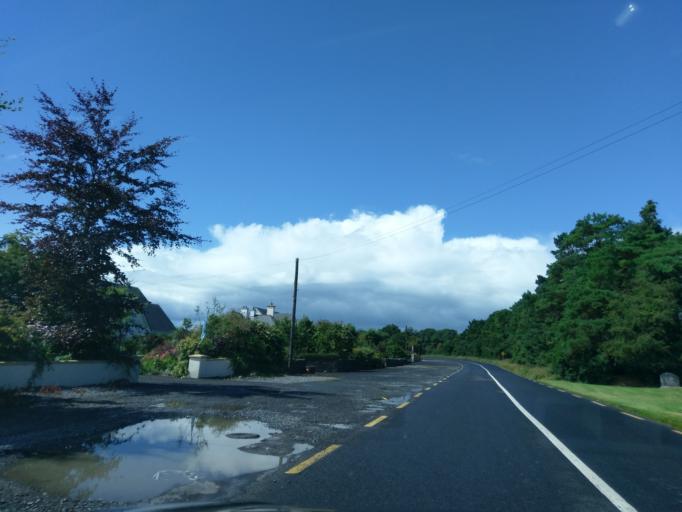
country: IE
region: Connaught
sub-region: County Galway
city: Oranmore
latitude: 53.2811
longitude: -8.8414
